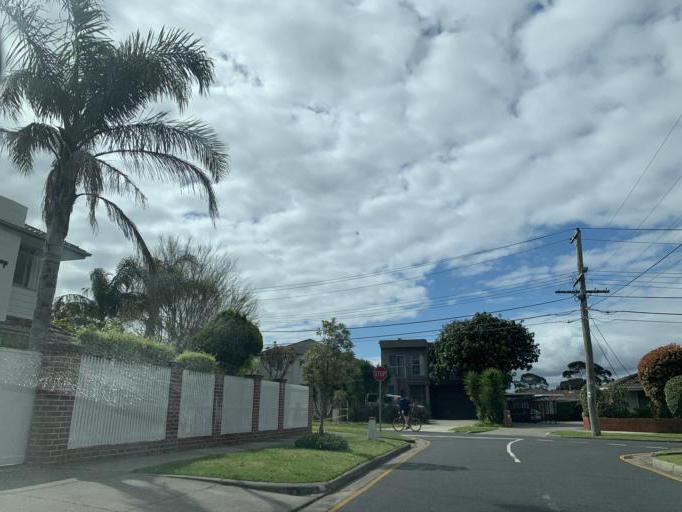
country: AU
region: Victoria
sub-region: Kingston
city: Mentone
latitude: -37.9828
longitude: 145.0535
